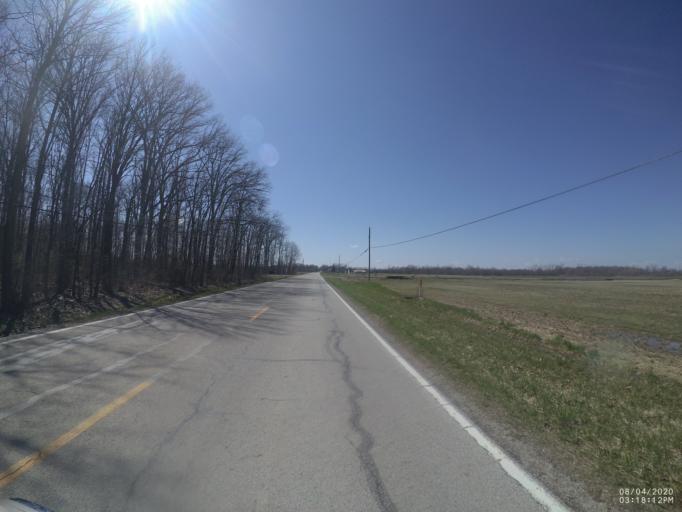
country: US
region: Ohio
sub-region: Sandusky County
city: Stony Prairie
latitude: 41.2674
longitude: -83.2363
